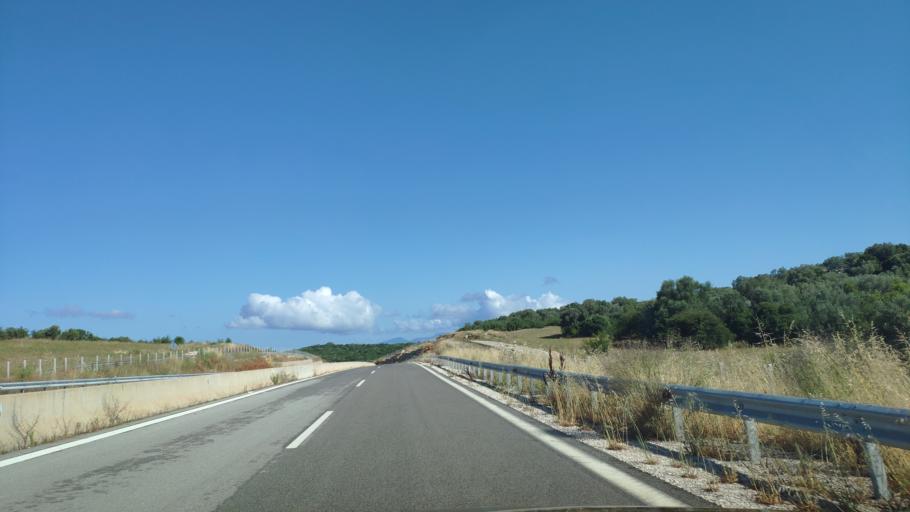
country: GR
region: West Greece
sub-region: Nomos Aitolias kai Akarnanias
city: Vonitsa
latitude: 38.9075
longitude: 20.8494
